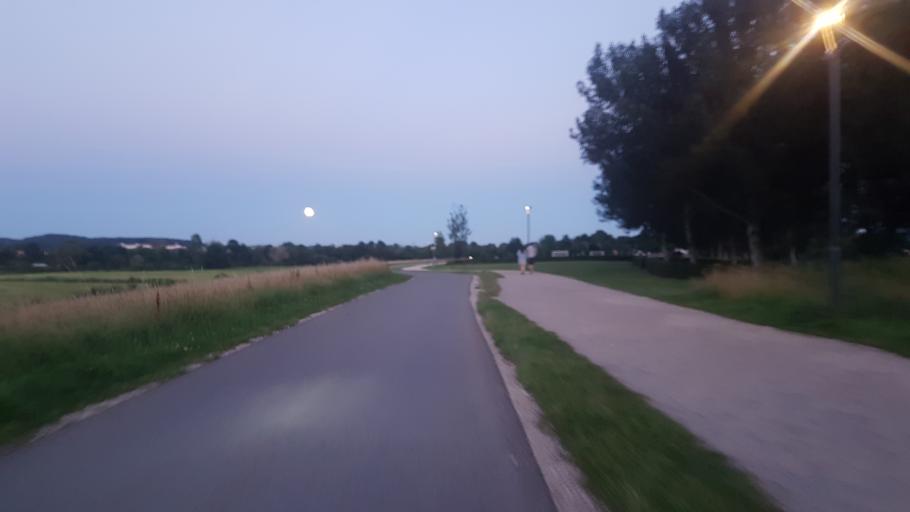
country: DE
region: Bavaria
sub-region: Regierungsbezirk Mittelfranken
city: Gunzenhausen
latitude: 49.1296
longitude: 10.7366
